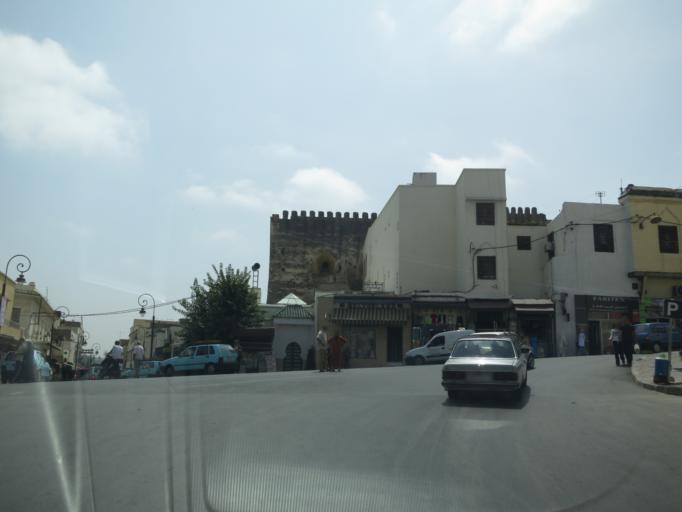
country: MA
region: Meknes-Tafilalet
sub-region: Meknes
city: Meknes
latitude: 33.8951
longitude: -5.5623
